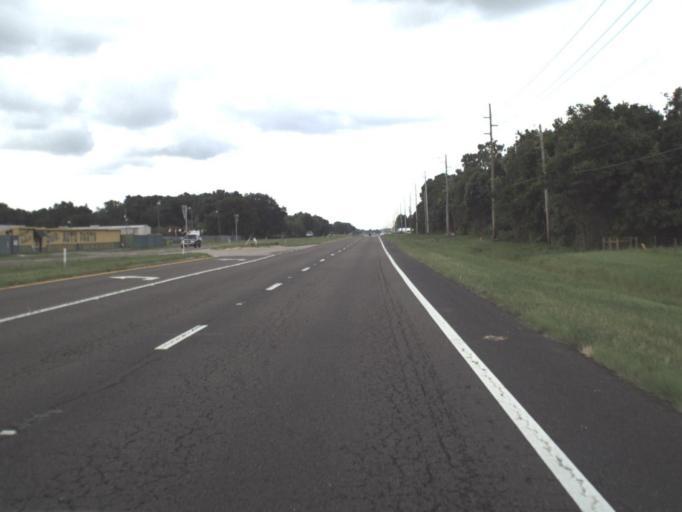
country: US
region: Florida
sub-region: Hillsborough County
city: Plant City
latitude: 27.9604
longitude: -82.1214
